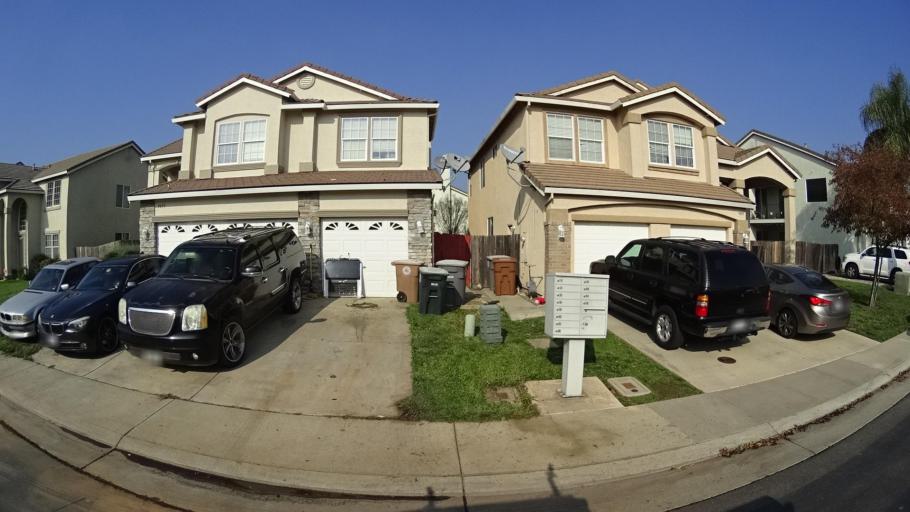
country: US
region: California
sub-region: Sacramento County
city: Elk Grove
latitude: 38.4174
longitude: -121.3460
